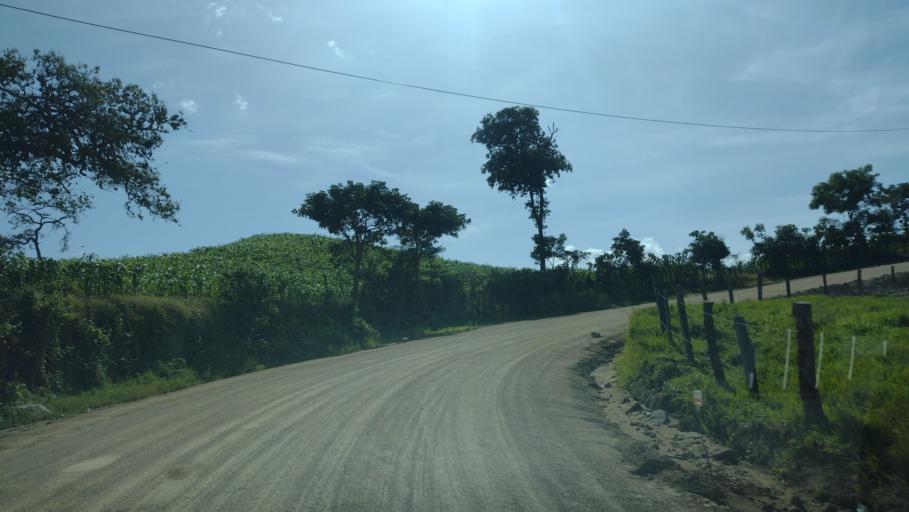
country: GT
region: Guatemala
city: Chinautla
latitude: 14.7529
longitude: -90.5147
